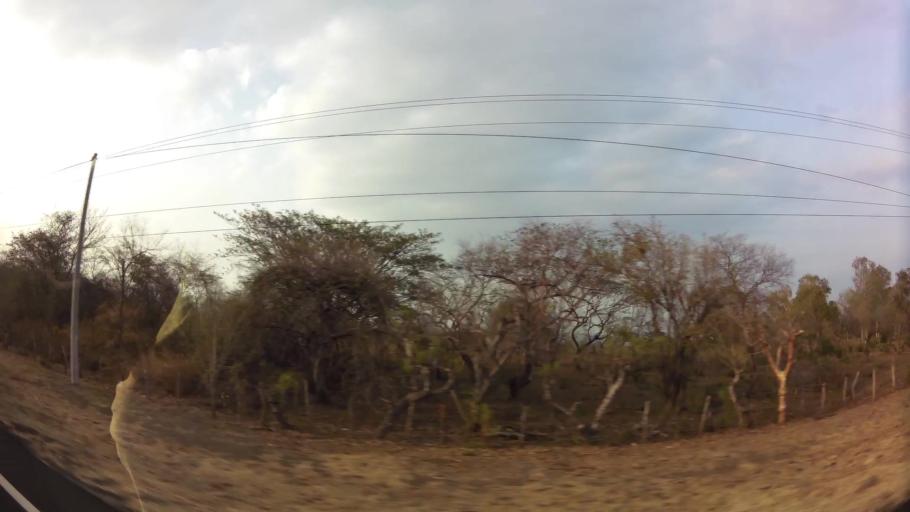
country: NI
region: Leon
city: Nagarote
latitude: 12.2757
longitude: -86.4964
